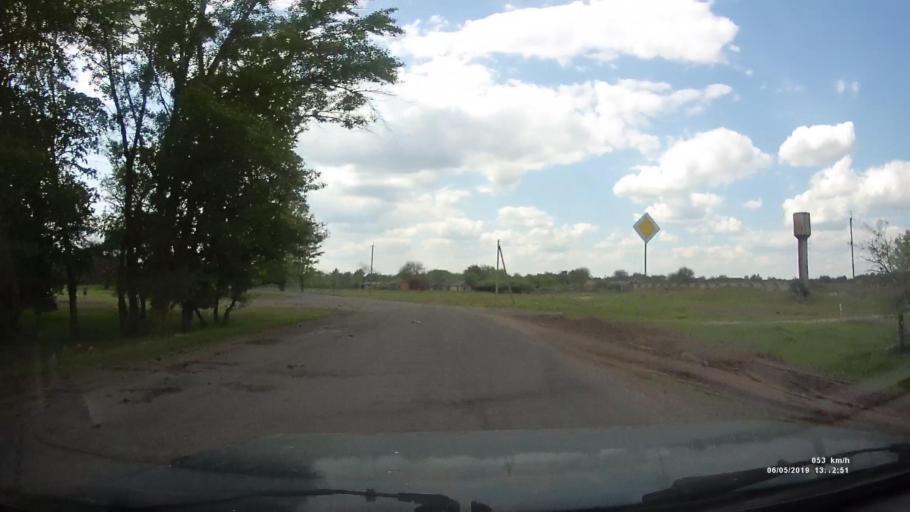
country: RU
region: Rostov
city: Ust'-Donetskiy
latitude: 47.7556
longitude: 40.9418
